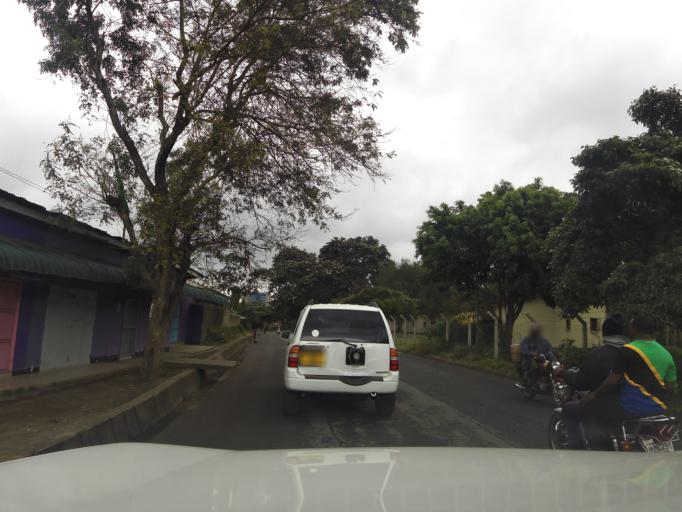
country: TZ
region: Arusha
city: Arusha
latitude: -3.3630
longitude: 36.6897
